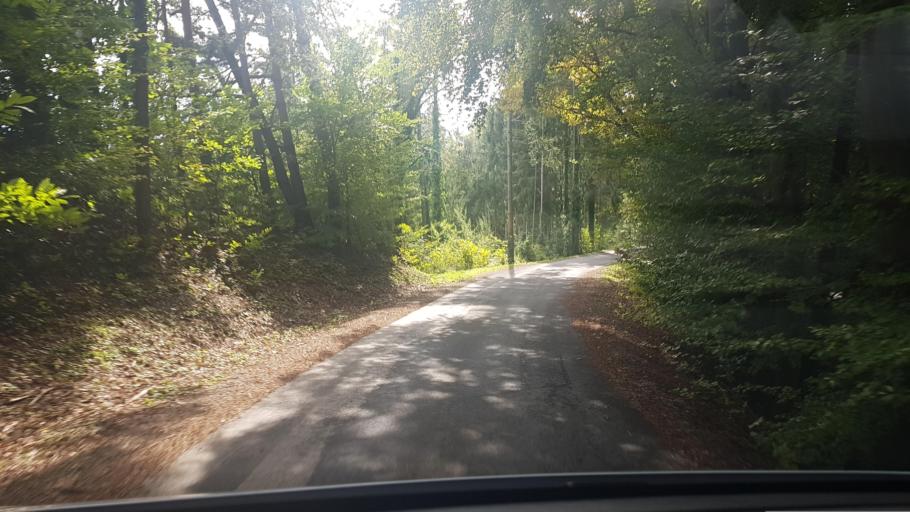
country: AT
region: Styria
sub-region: Politischer Bezirk Leibnitz
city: Sankt Johann im Saggautal
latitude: 46.7067
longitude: 15.4317
